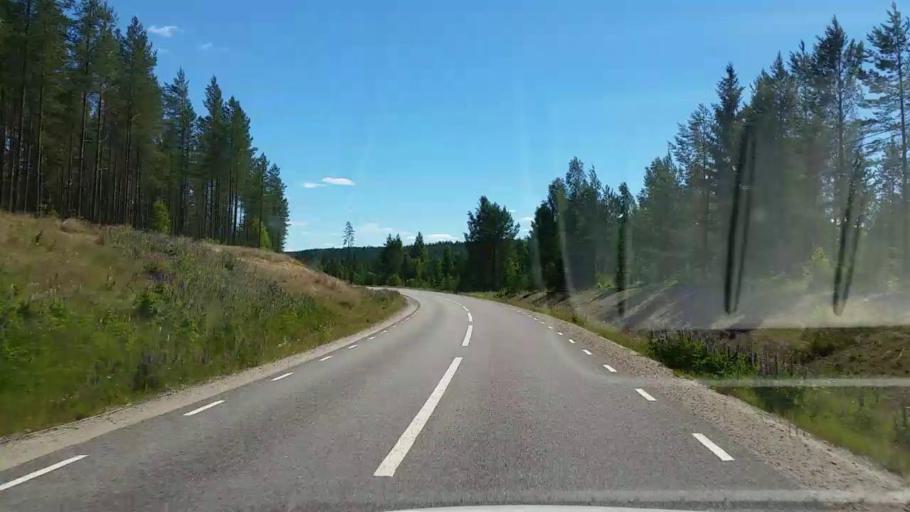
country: SE
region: Gaevleborg
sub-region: Ovanakers Kommun
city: Edsbyn
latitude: 61.4288
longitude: 15.7203
